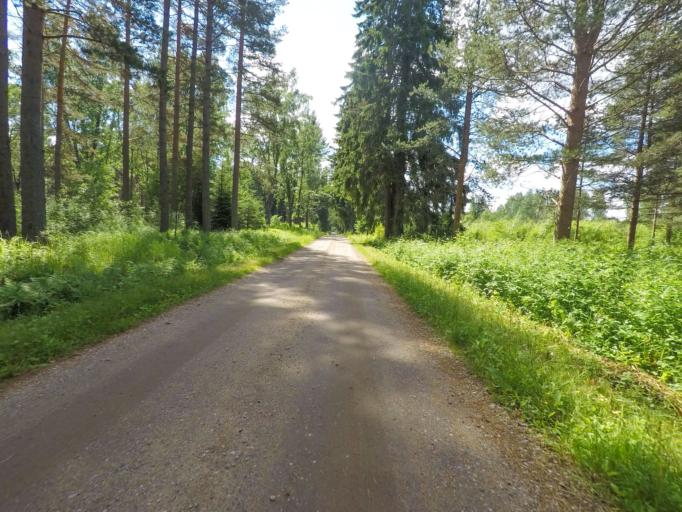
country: FI
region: Southern Savonia
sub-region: Savonlinna
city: Punkaharju
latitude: 61.8051
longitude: 29.3206
